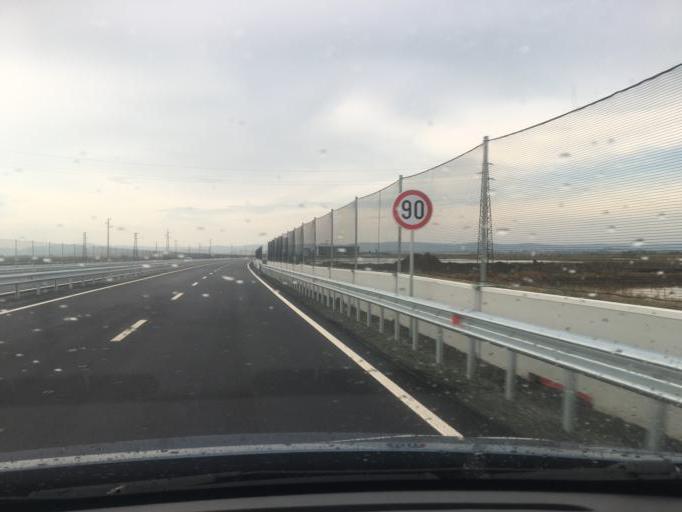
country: BG
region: Burgas
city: Aheloy
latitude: 42.6168
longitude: 27.6249
